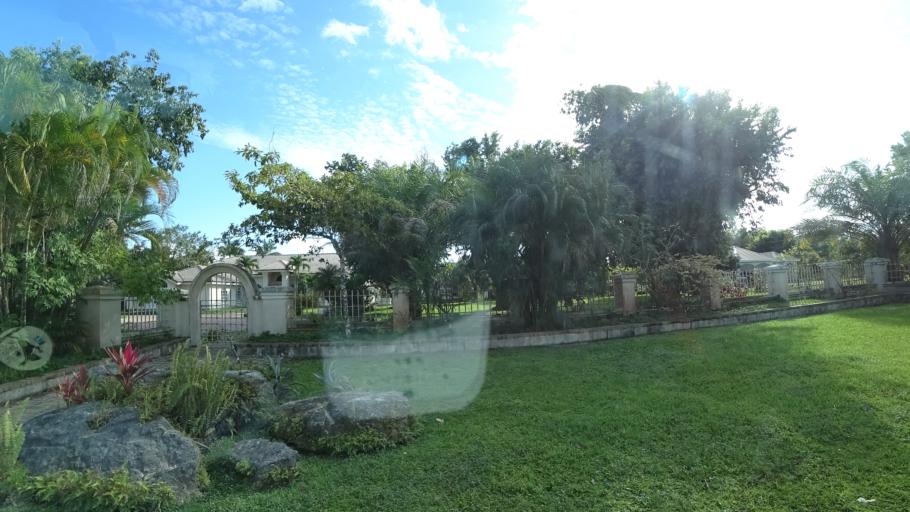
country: BZ
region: Belize
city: Belize City
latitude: 17.5566
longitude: -88.4036
